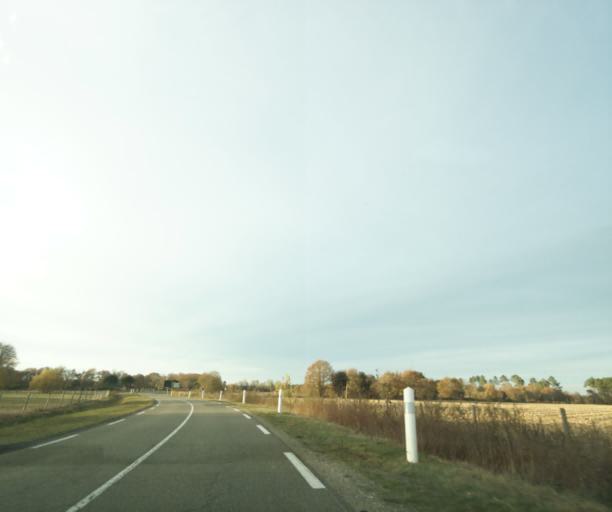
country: FR
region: Aquitaine
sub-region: Departement des Landes
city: Gabarret
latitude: 44.1107
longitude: -0.0998
